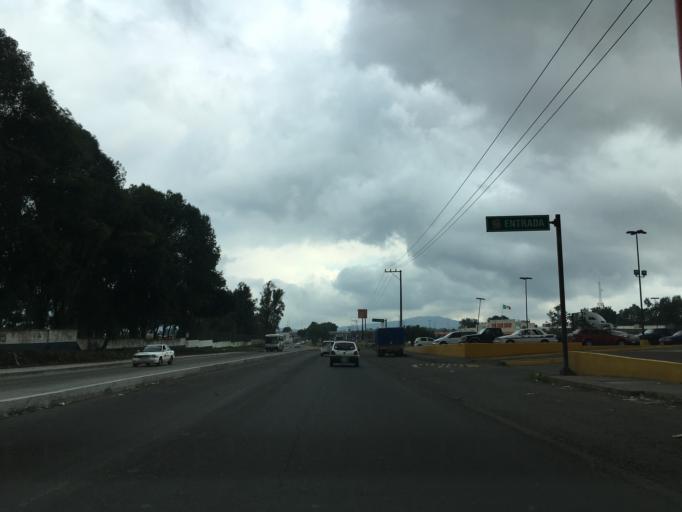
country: MX
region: Michoacan
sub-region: Uruapan
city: Toreo Bajo (El Toreo Bajo)
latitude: 19.4269
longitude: -102.0252
